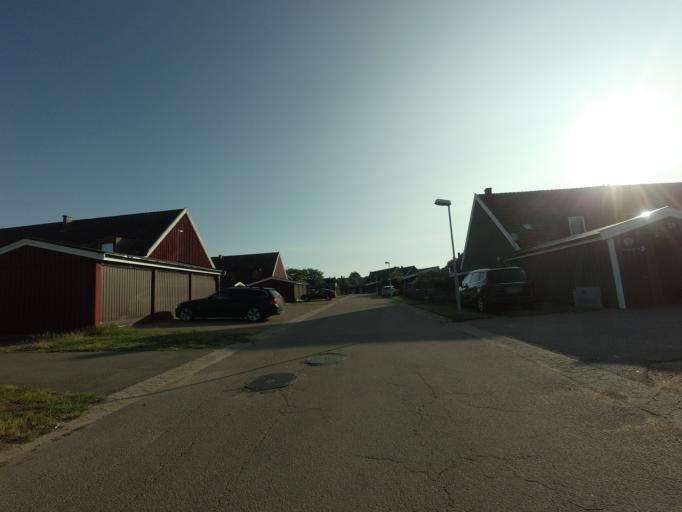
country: SE
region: Skane
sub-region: Landskrona
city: Asmundtorp
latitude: 55.8480
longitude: 12.9273
